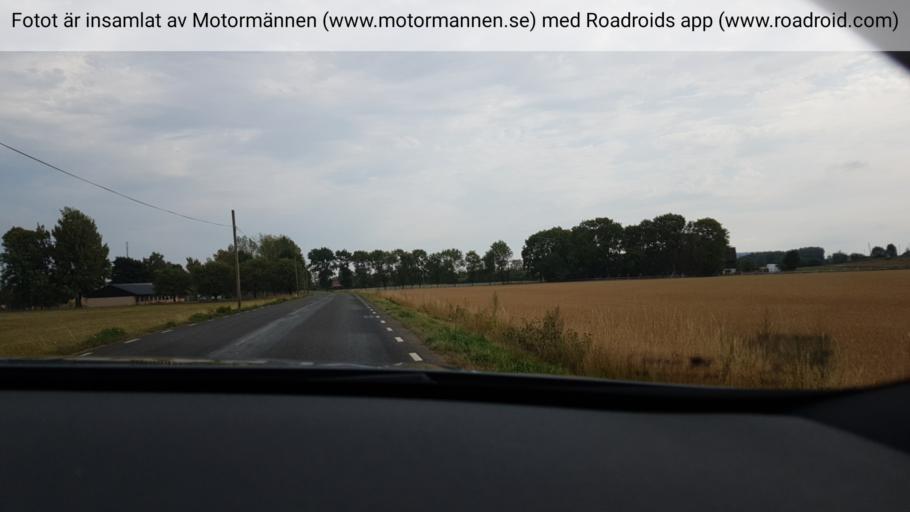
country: SE
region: Vaestra Goetaland
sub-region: Falkopings Kommun
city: Akarp
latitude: 58.1873
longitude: 13.6289
